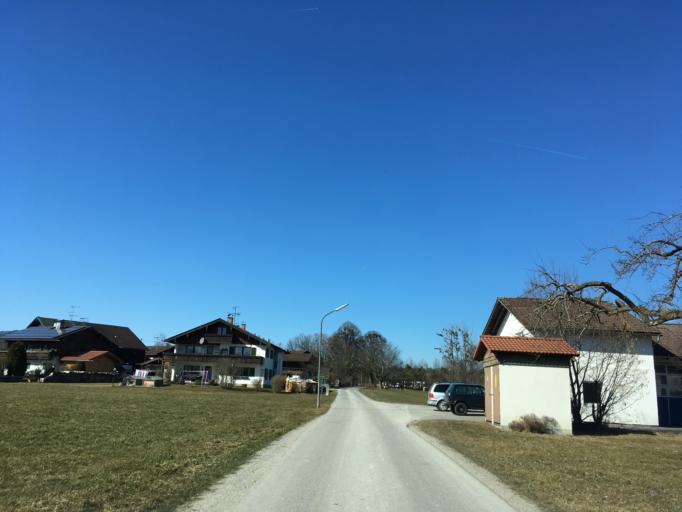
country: DE
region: Bavaria
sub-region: Upper Bavaria
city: Bad Aibling
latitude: 47.8232
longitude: 11.9795
